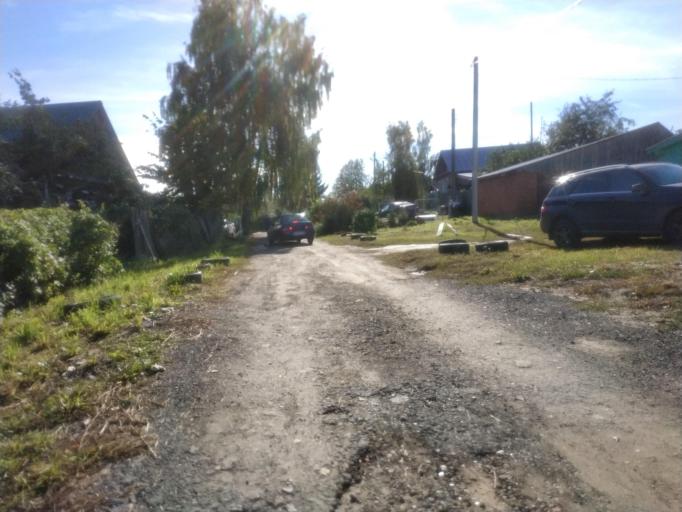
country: RU
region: Chuvashia
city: Novyye Lapsary
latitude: 56.1446
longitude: 47.1496
